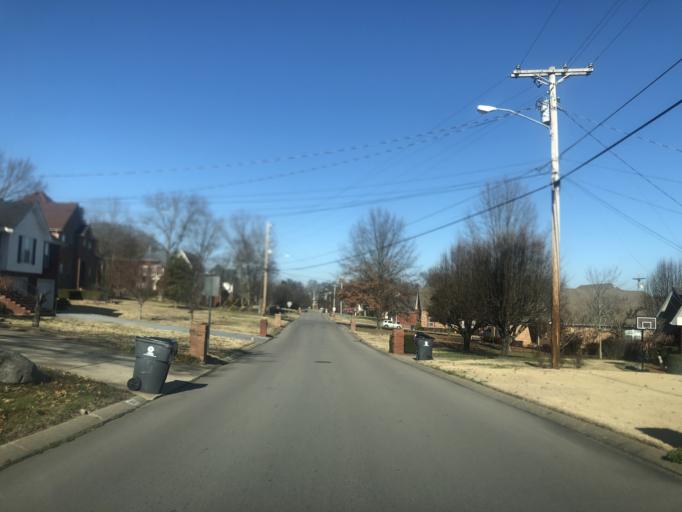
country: US
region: Tennessee
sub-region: Rutherford County
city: Smyrna
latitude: 35.9720
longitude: -86.5404
